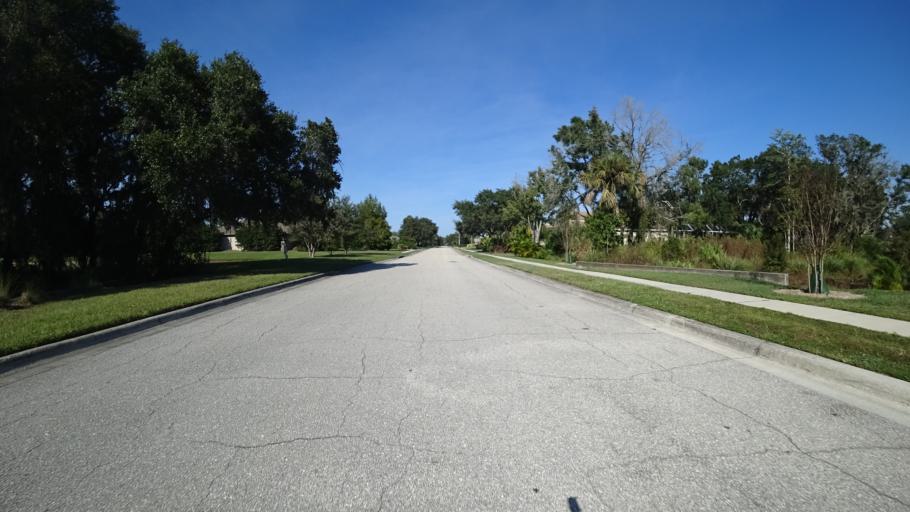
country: US
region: Florida
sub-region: Sarasota County
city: The Meadows
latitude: 27.4123
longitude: -82.4451
